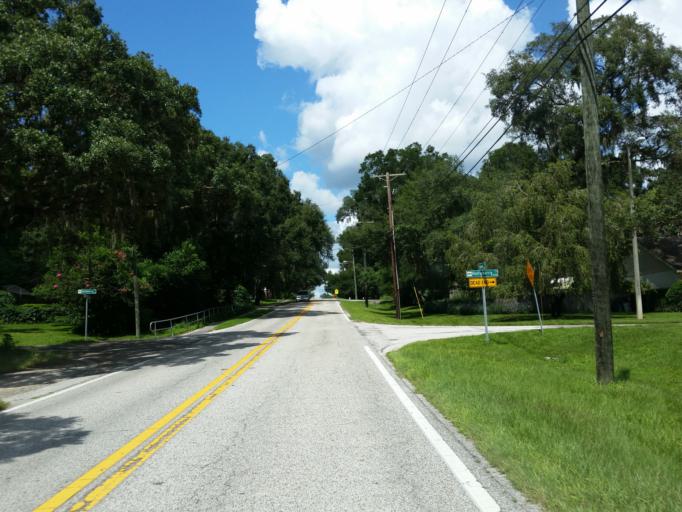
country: US
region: Florida
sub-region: Hillsborough County
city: Bloomingdale
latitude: 27.9048
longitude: -82.2692
